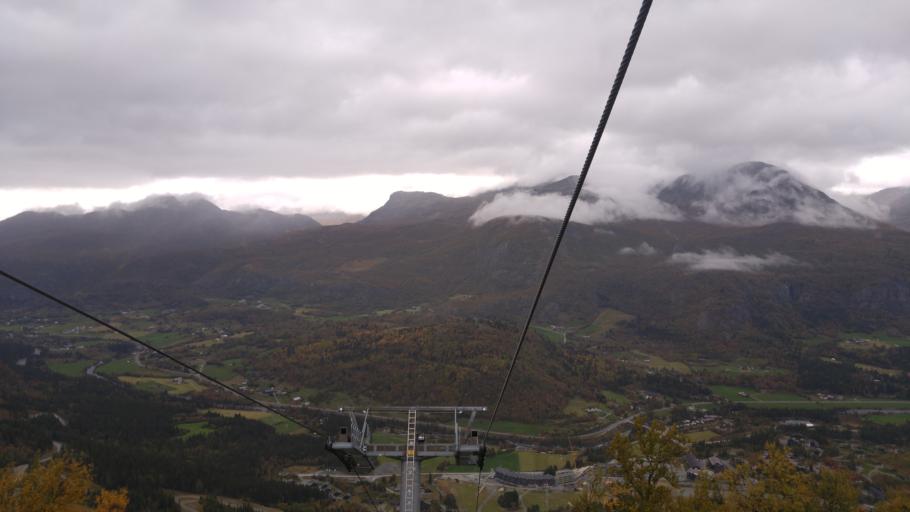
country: NO
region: Buskerud
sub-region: Hemsedal
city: Hemsedal
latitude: 60.8523
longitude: 8.5121
